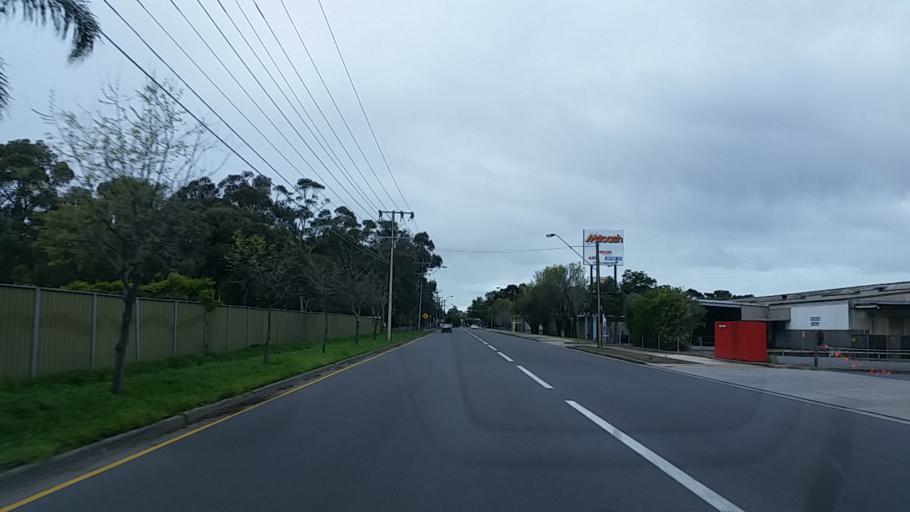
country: AU
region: South Australia
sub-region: Charles Sturt
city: Findon
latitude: -34.9154
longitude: 138.5346
